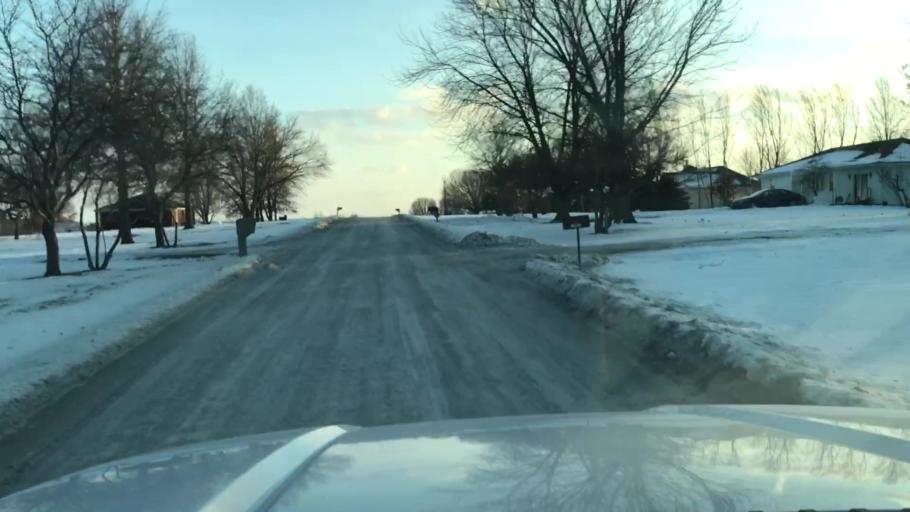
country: US
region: Missouri
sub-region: Clinton County
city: Cameron
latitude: 39.7299
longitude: -94.2128
